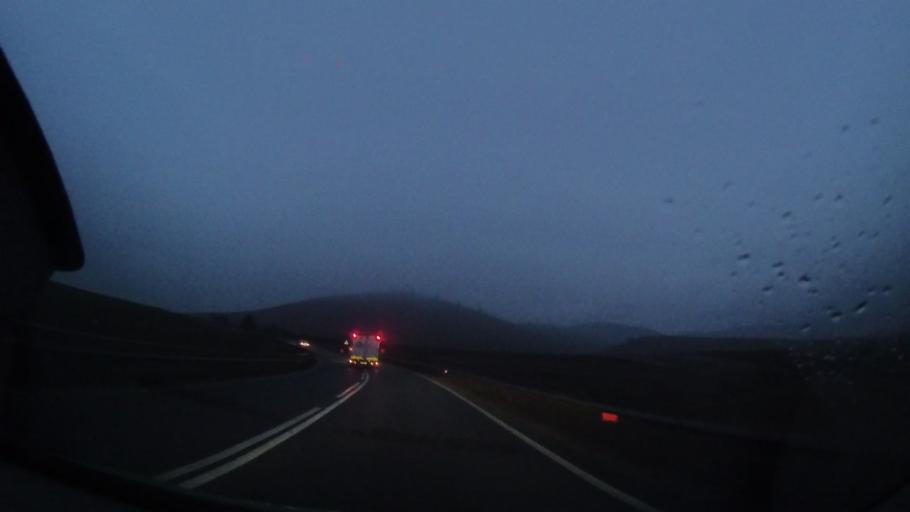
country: RO
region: Harghita
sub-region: Comuna Ditrau
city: Ditrau
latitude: 46.8365
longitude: 25.4897
